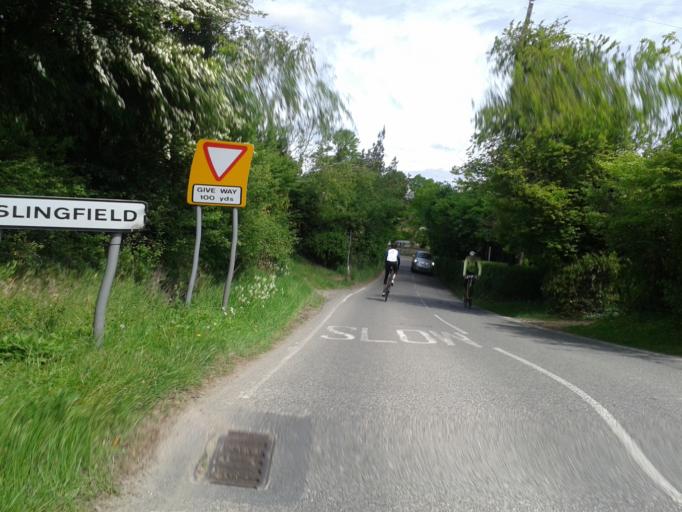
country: GB
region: England
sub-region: Cambridgeshire
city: Haslingfield
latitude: 52.1484
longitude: 0.0500
